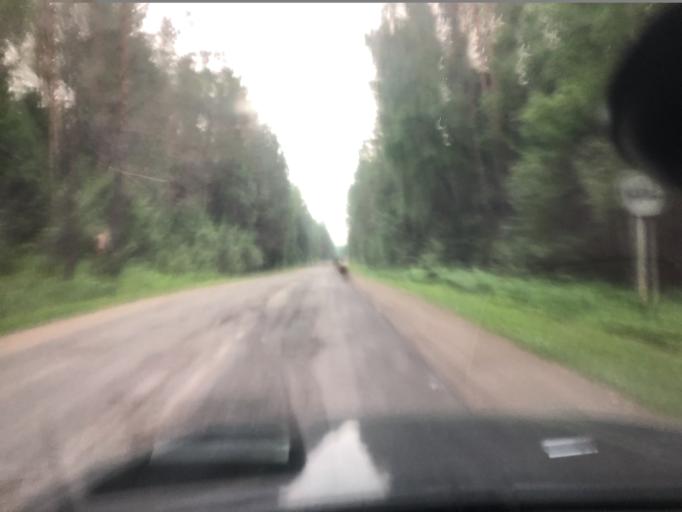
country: RU
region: Jaroslavl
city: Petrovsk
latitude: 57.0001
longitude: 39.0791
